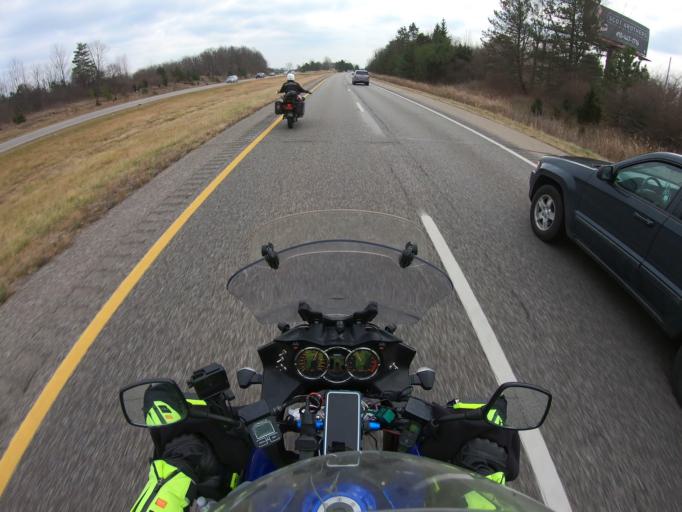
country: US
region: Michigan
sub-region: Genesee County
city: Grand Blanc
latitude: 42.9272
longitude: -83.6908
